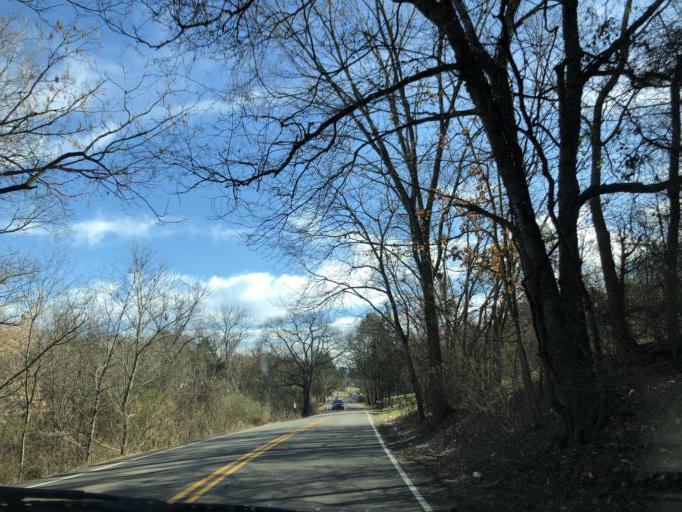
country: US
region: Tennessee
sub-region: Wilson County
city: Green Hill
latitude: 36.1721
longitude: -86.5660
